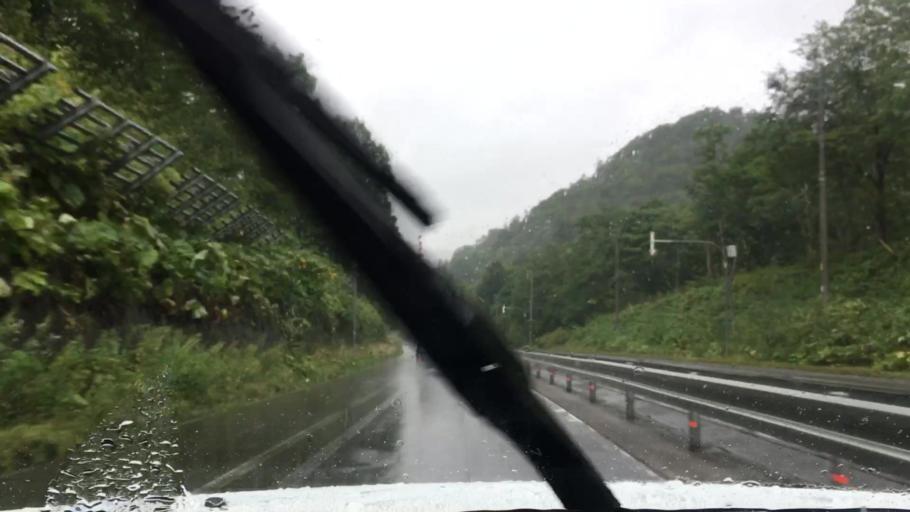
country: JP
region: Hokkaido
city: Otaru
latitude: 42.8468
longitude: 141.0537
